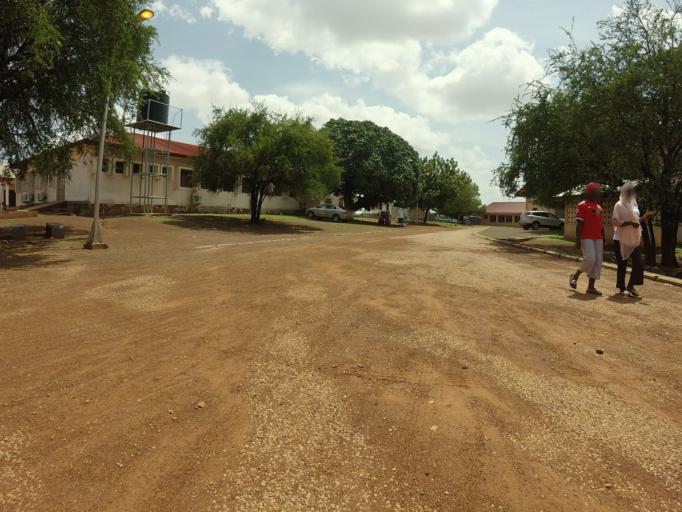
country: GH
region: Northern
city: Tamale
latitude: 9.3922
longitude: -0.8247
